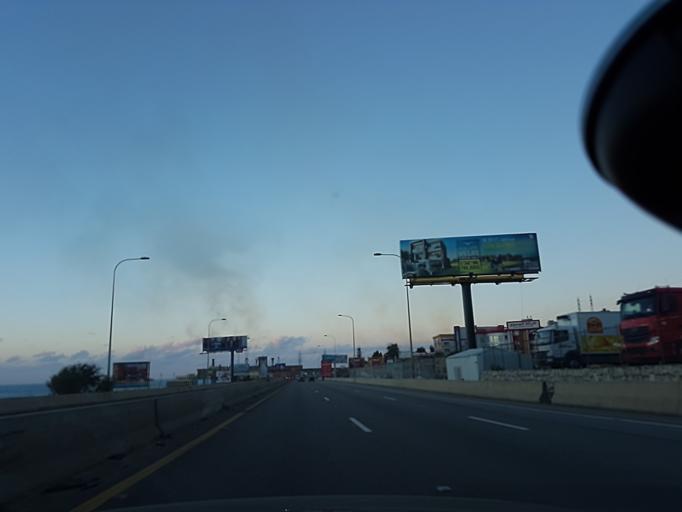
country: LB
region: Liban-Sud
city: Sidon
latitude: 33.6410
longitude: 35.4025
